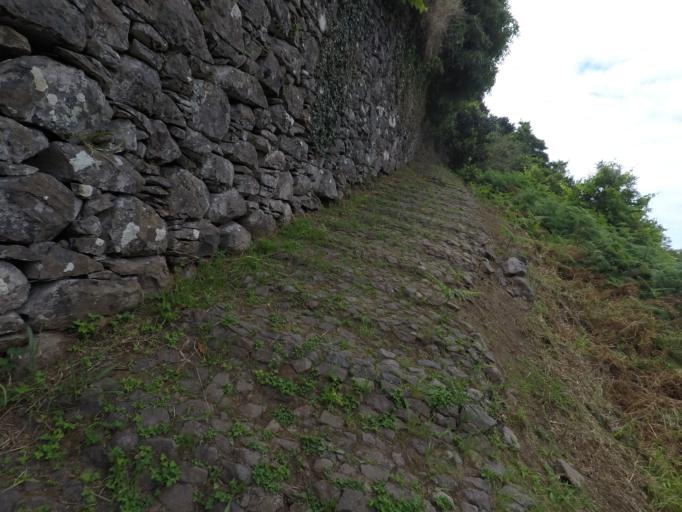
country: PT
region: Madeira
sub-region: Sao Vicente
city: Sao Vicente
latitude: 32.8188
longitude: -16.9698
